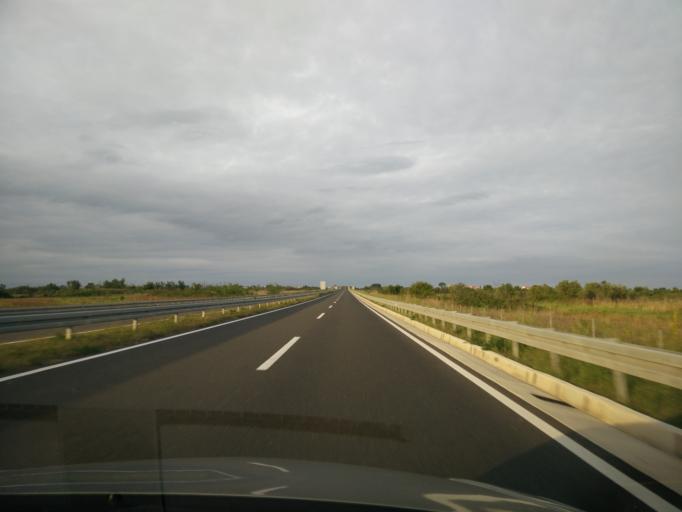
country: HR
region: Zadarska
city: Galovac
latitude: 44.1152
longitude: 15.4083
